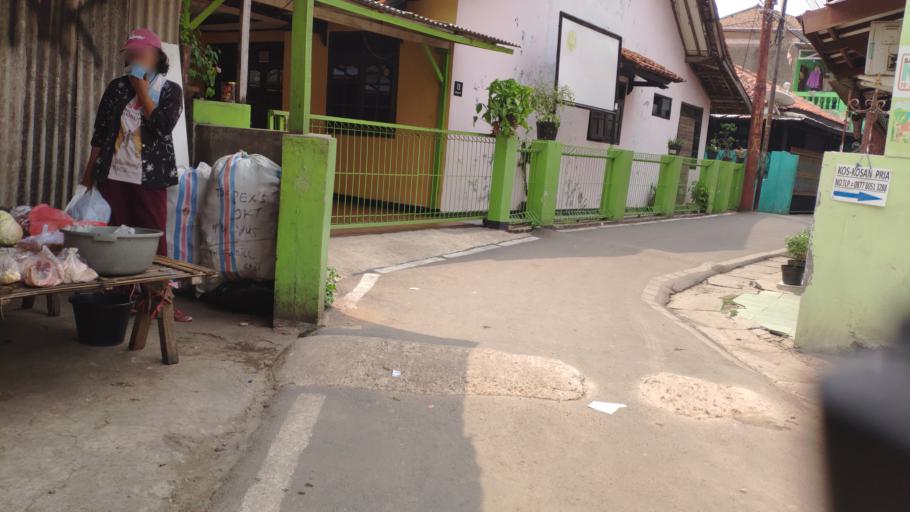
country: ID
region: Jakarta Raya
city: Jakarta
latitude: -6.3044
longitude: 106.8282
